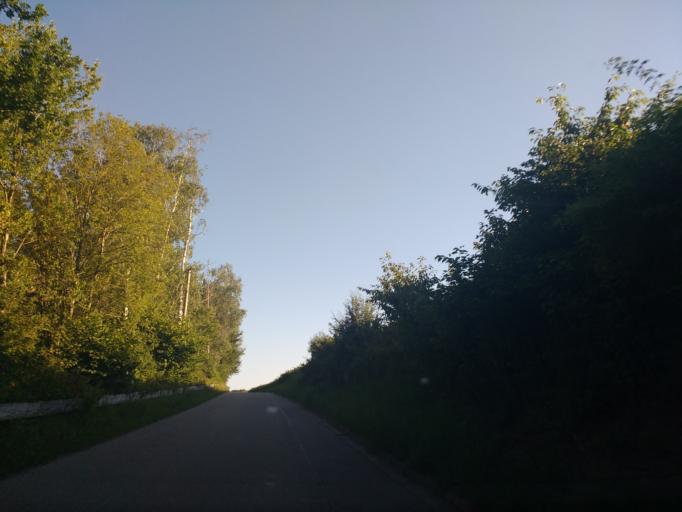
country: DE
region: Bavaria
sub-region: Upper Bavaria
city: Oberneukirchen
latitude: 48.1957
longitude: 12.4860
